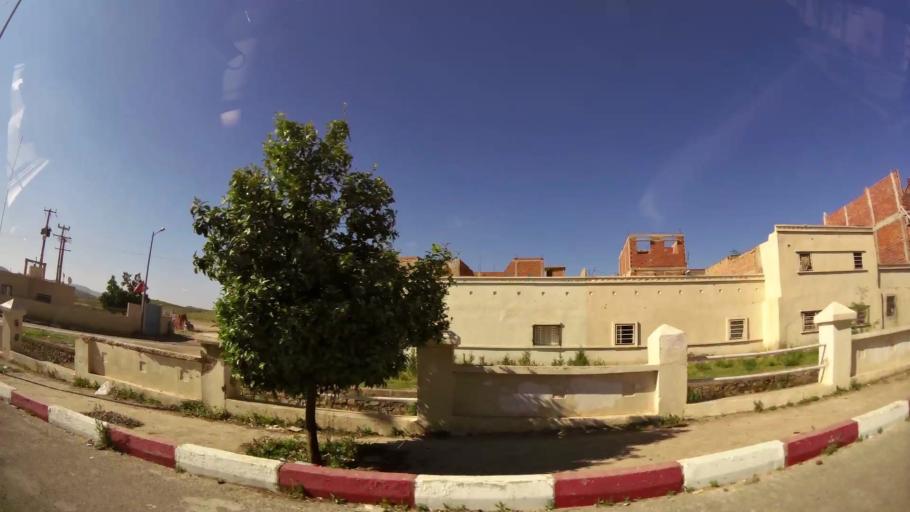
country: MA
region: Oriental
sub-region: Oujda-Angad
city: Oujda
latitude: 34.6507
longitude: -1.9405
